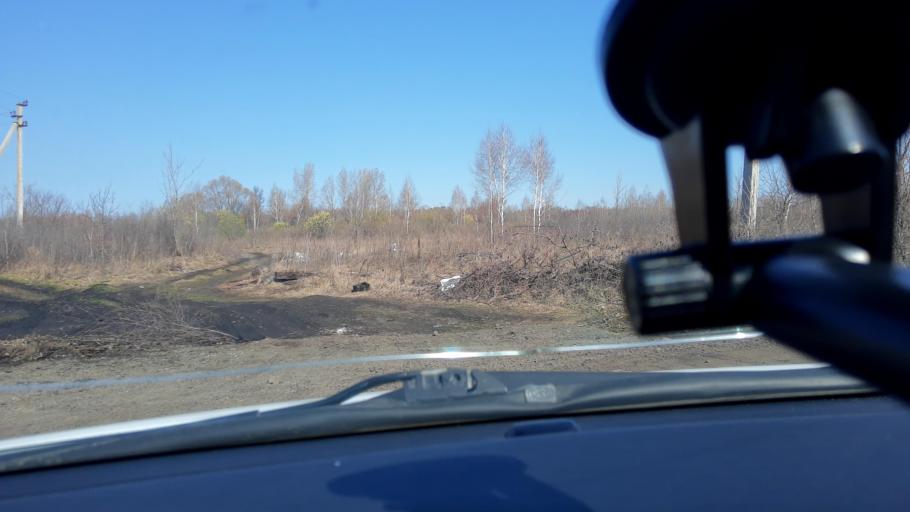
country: RU
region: Bashkortostan
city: Mikhaylovka
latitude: 54.7210
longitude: 55.8229
